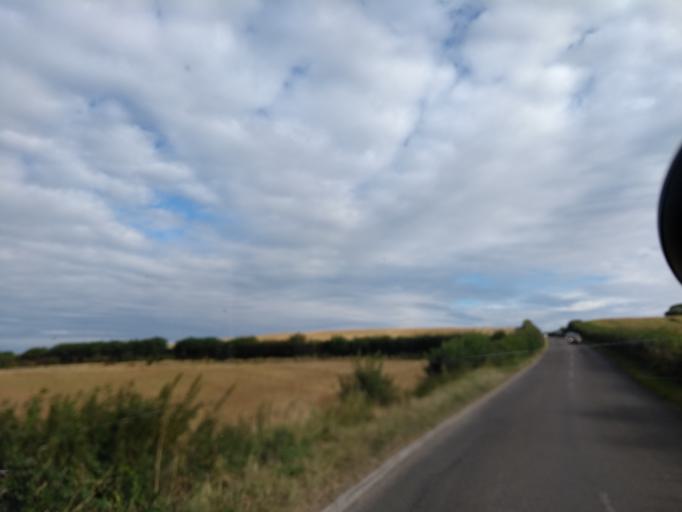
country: GB
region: England
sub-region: Somerset
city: Ilminster
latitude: 50.9075
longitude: -2.8648
